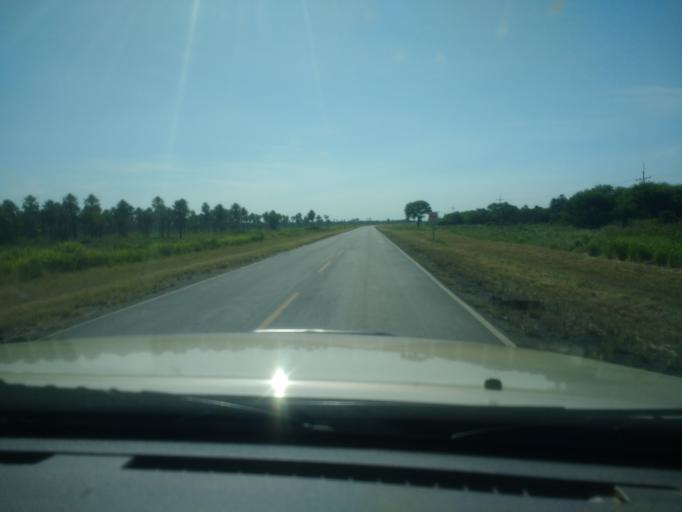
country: PY
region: Presidente Hayes
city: Benjamin Aceval
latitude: -24.9099
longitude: -57.6340
